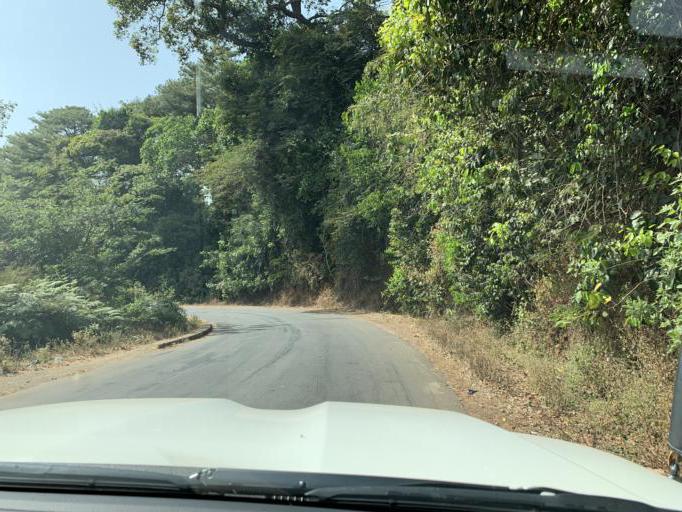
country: GN
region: Mamou
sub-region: Dalaba
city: Dalaba
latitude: 10.7127
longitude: -12.2520
